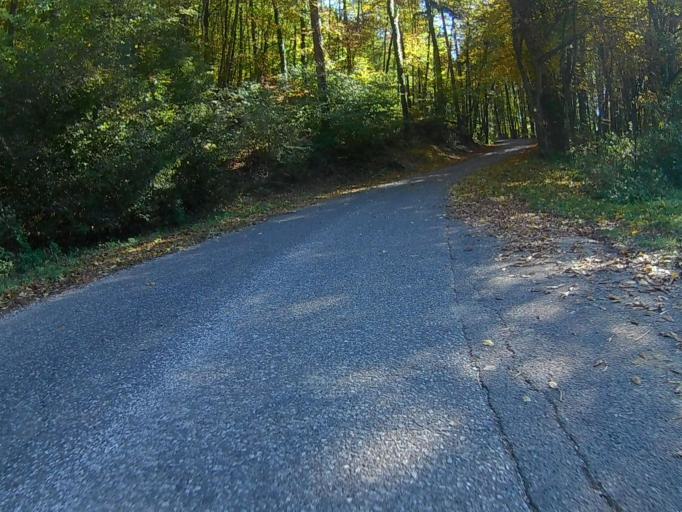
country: SI
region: Duplek
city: Spodnji Duplek
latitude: 46.5457
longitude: 15.7802
